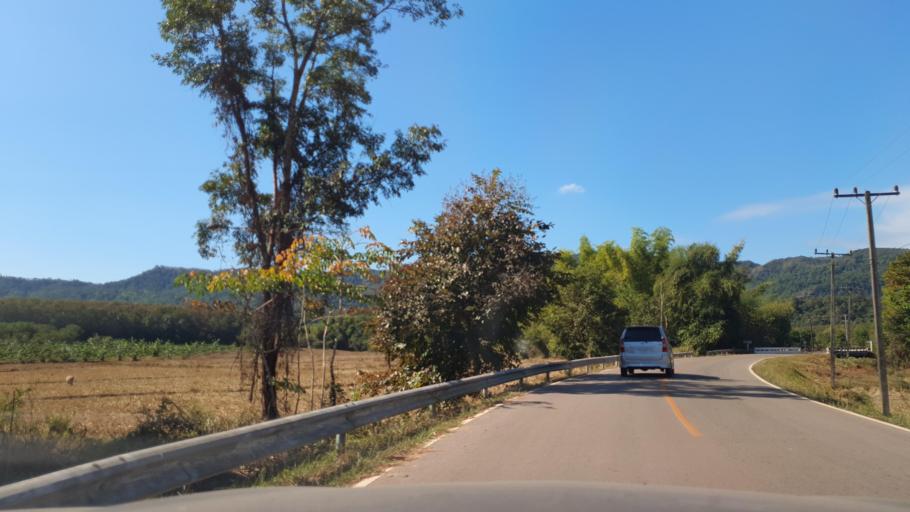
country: TH
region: Nakhon Phanom
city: Ban Phaeng
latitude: 17.9892
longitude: 104.1518
